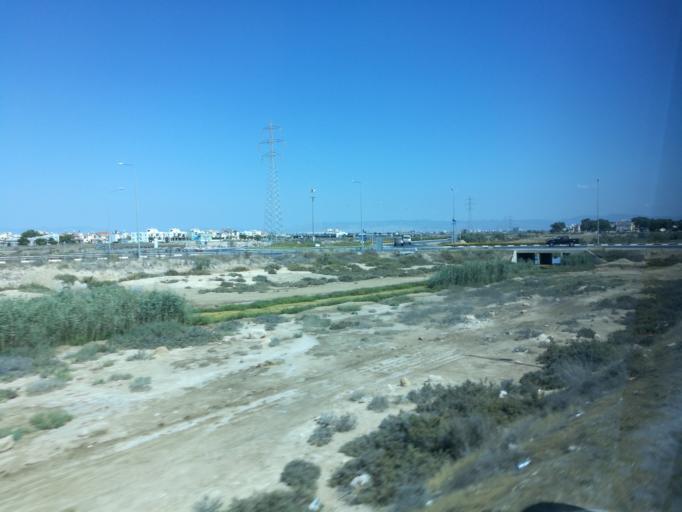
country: CY
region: Ammochostos
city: Famagusta
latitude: 35.1547
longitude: 33.9013
